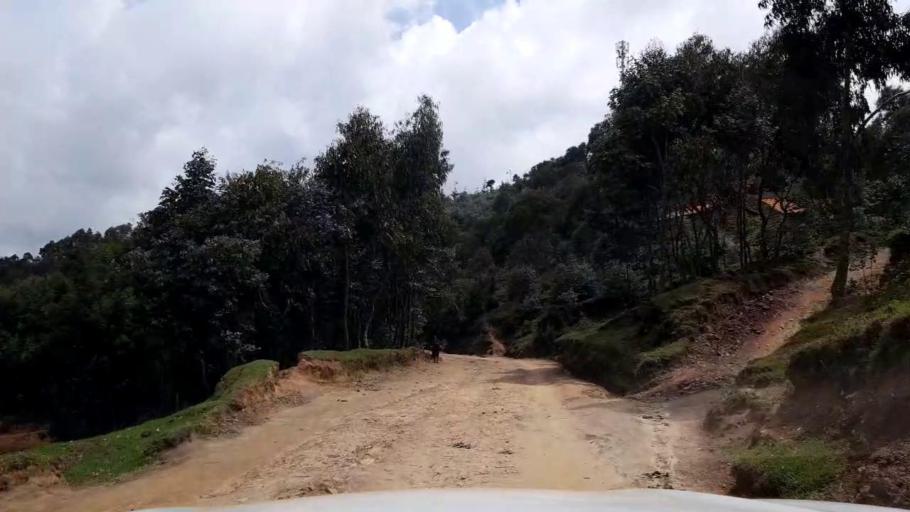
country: RW
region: Western Province
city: Kibuye
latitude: -1.9349
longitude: 29.4526
